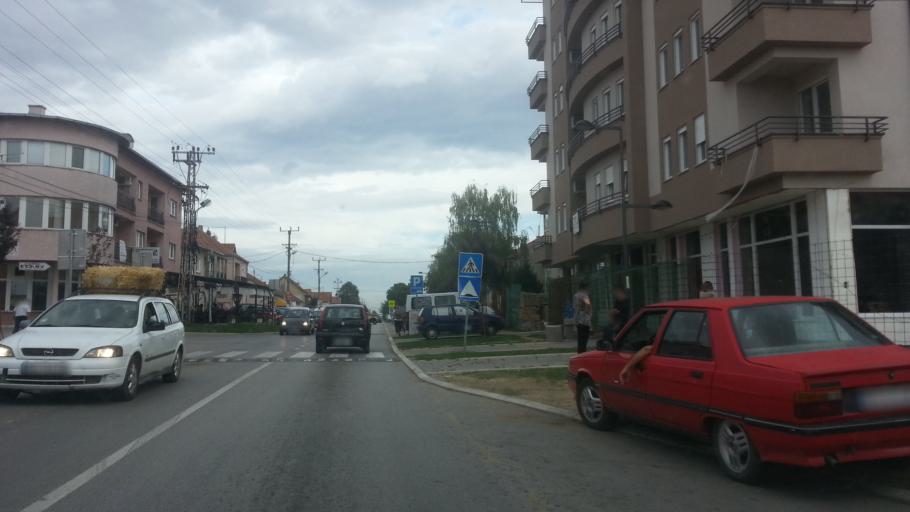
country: RS
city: Novi Banovci
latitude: 44.9556
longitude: 20.2807
